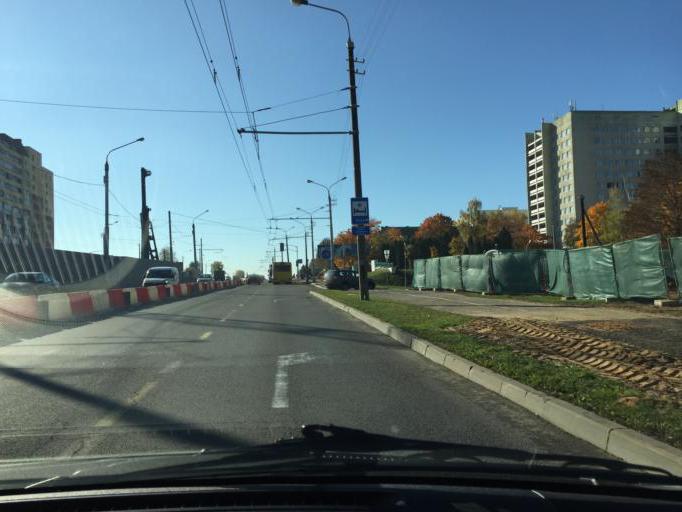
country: BY
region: Minsk
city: Syenitsa
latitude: 53.8536
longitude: 27.5380
